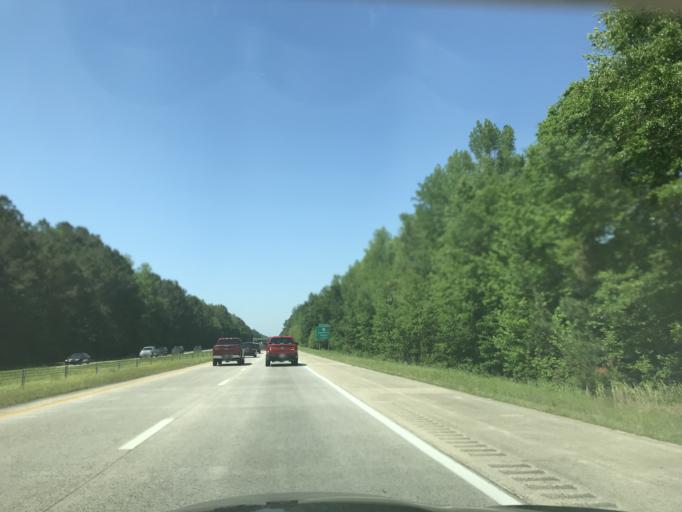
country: US
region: North Carolina
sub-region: Johnston County
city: Benson
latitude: 35.4833
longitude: -78.5511
